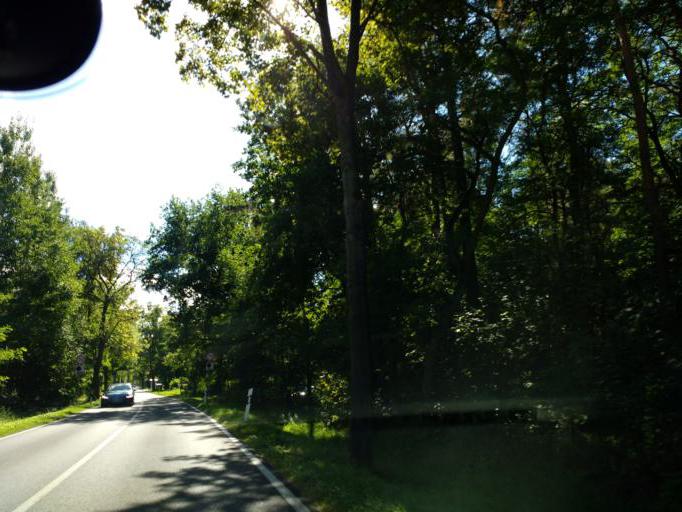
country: DE
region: Brandenburg
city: Mittenwalde
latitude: 52.2252
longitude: 13.5744
